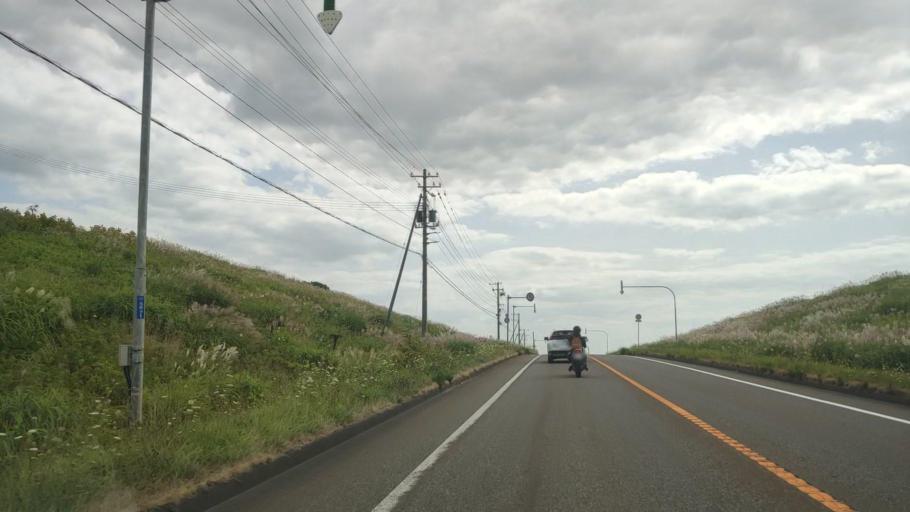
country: JP
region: Hokkaido
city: Rumoi
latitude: 44.5215
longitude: 141.7655
